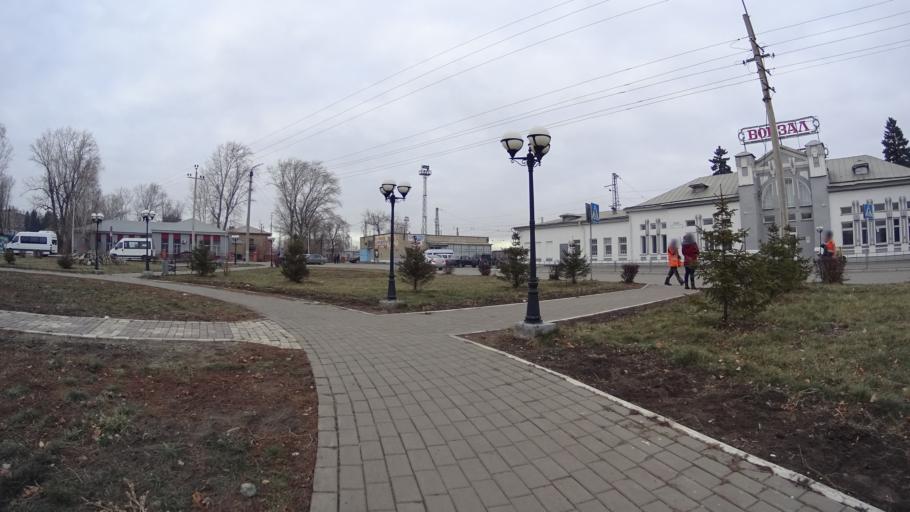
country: RU
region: Chelyabinsk
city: Troitsk
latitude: 54.1130
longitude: 61.5693
